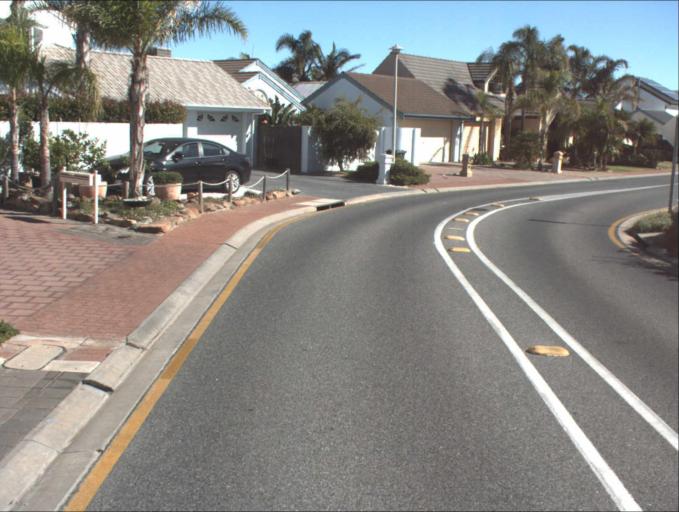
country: AU
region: South Australia
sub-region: Port Adelaide Enfield
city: Birkenhead
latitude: -34.7824
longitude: 138.4819
